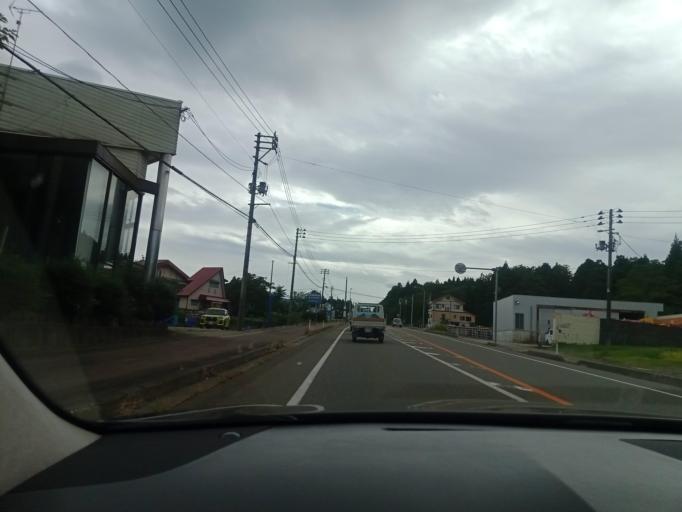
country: JP
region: Niigata
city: Arai
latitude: 36.9484
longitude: 138.2192
